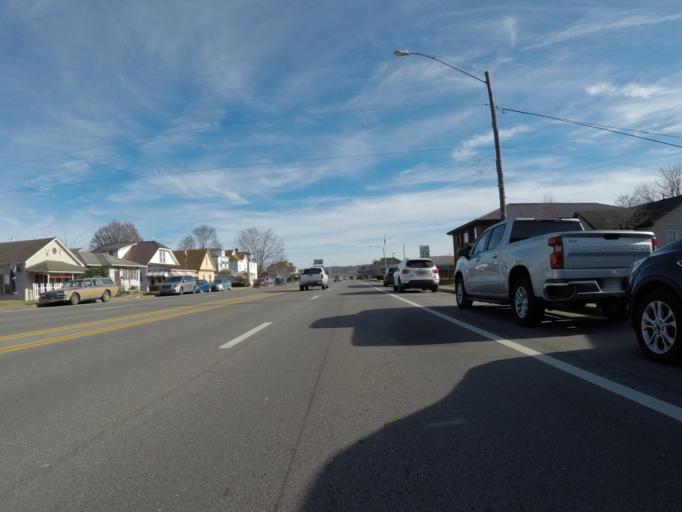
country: US
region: West Virginia
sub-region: Wayne County
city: Kenova
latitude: 38.4004
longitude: -82.5752
